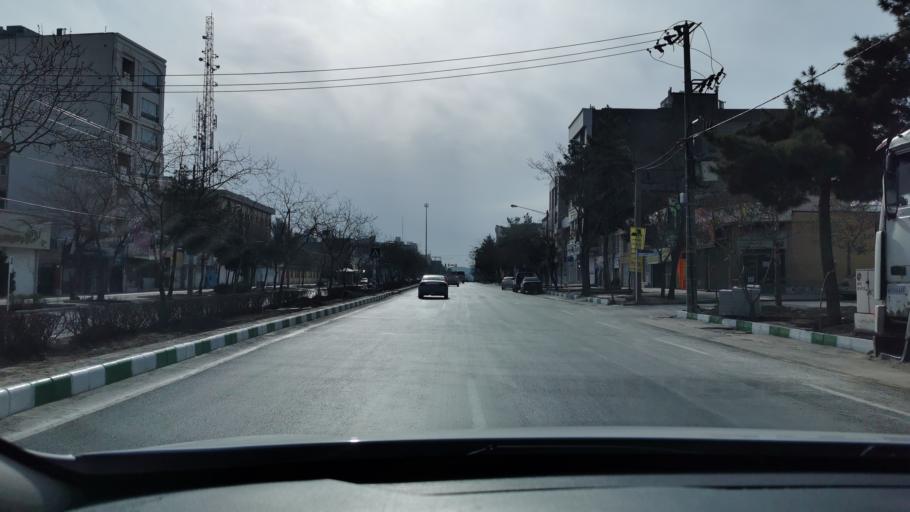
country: IR
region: Razavi Khorasan
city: Mashhad
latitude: 36.2921
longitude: 59.5357
